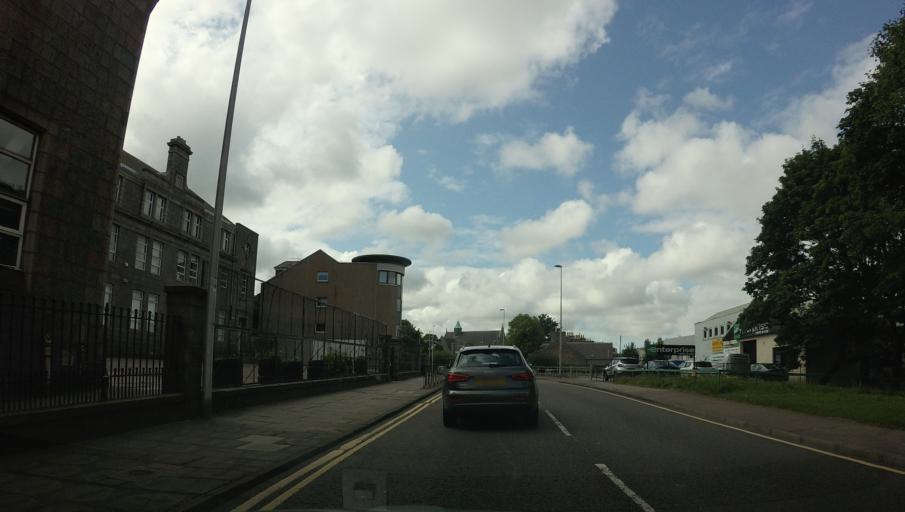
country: GB
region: Scotland
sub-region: Aberdeen City
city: Aberdeen
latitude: 57.1519
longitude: -2.1100
